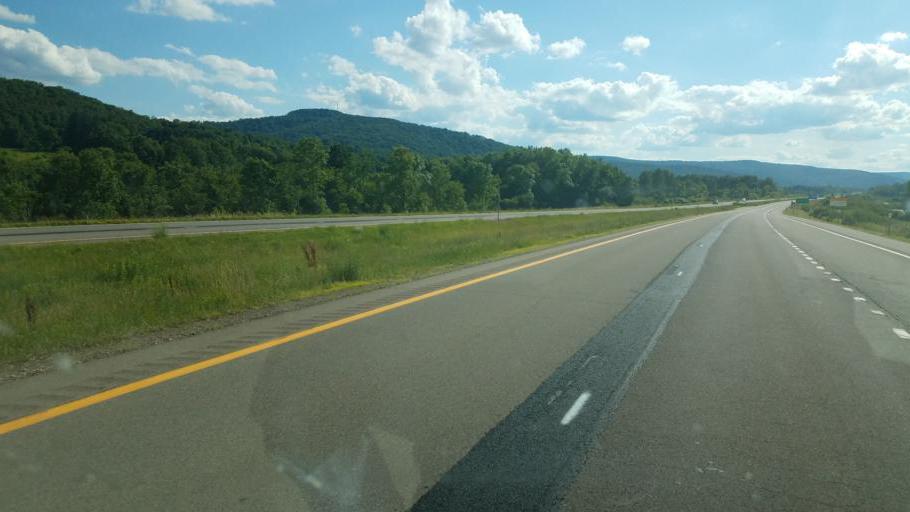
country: US
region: New York
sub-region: Cattaraugus County
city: Allegany
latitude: 42.0935
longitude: -78.5409
